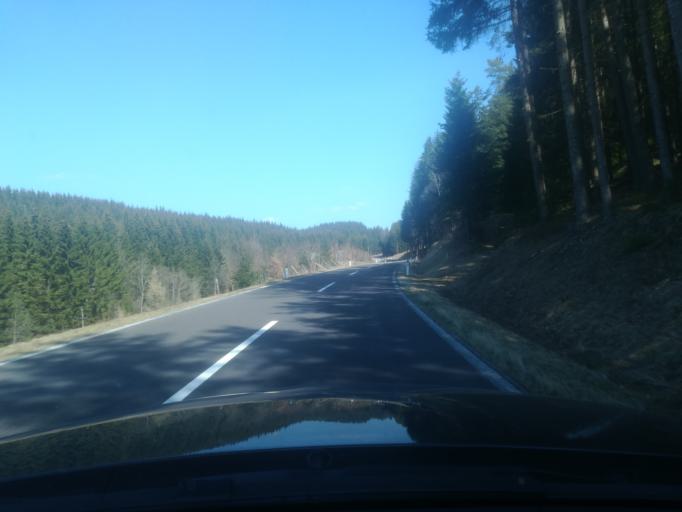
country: AT
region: Lower Austria
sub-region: Politischer Bezirk Zwettl
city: Langschlag
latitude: 48.4984
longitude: 14.8241
